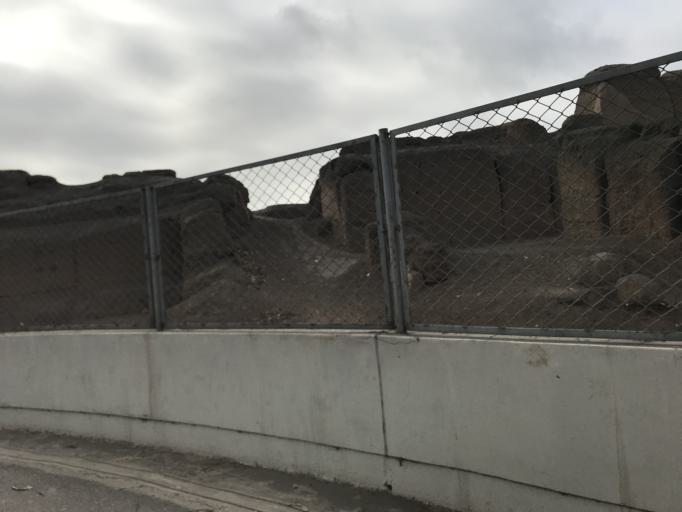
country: PE
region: Callao
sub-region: Callao
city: Callao
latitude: -12.0675
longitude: -77.0897
